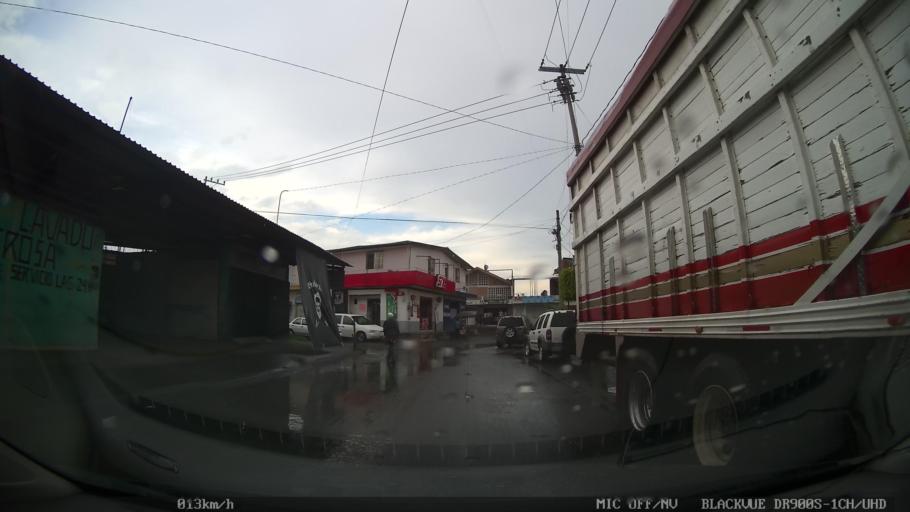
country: MX
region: Michoacan
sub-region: Uruapan
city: Santa Rosa (Santa Barbara)
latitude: 19.4049
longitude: -102.0251
